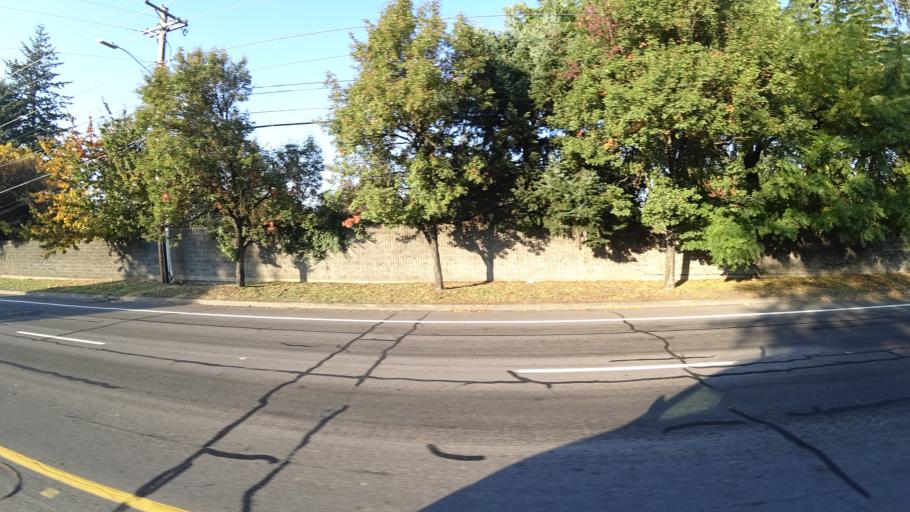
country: US
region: Oregon
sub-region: Multnomah County
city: Gresham
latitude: 45.5139
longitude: -122.4504
